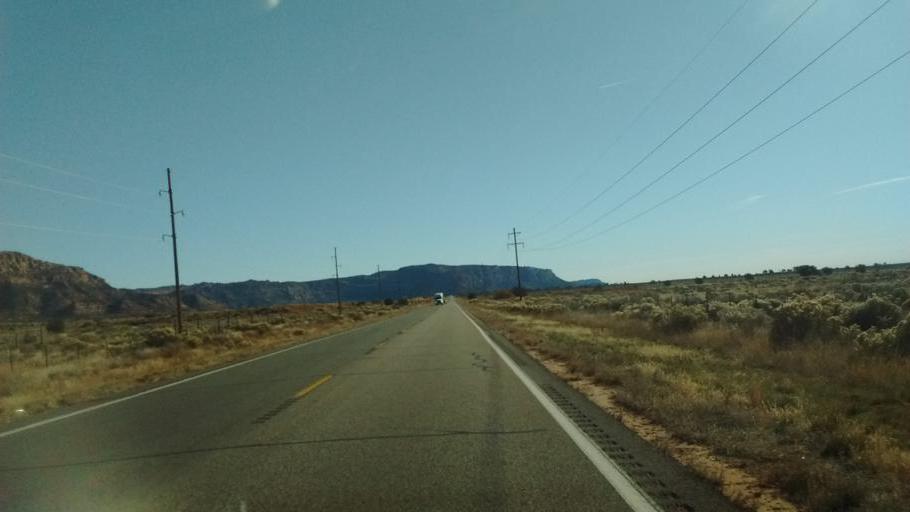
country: US
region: Arizona
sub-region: Mohave County
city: Colorado City
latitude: 37.0159
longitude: -113.0265
